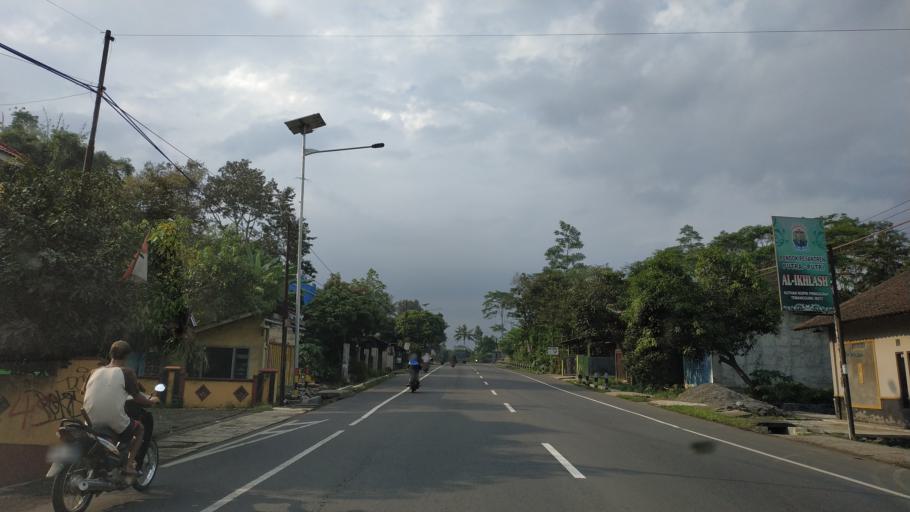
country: ID
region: Central Java
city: Gunung Kendil
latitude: -7.3415
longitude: 110.3213
